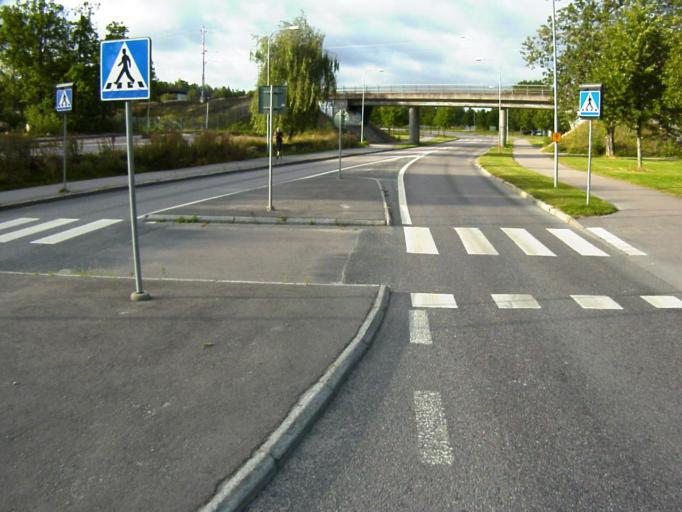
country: SE
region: Soedermanland
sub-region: Eskilstuna Kommun
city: Eskilstuna
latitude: 59.3622
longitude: 16.5308
